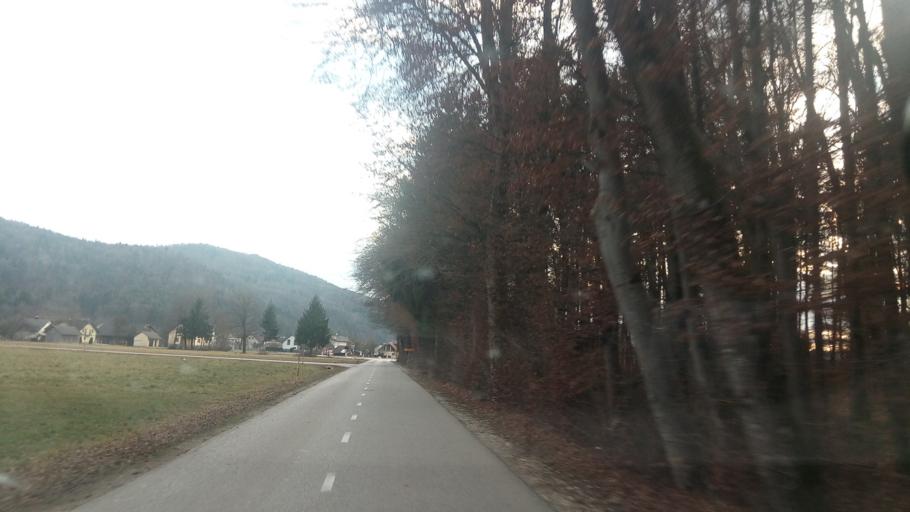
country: SI
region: Vodice
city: Vodice
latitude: 46.1655
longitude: 14.5181
